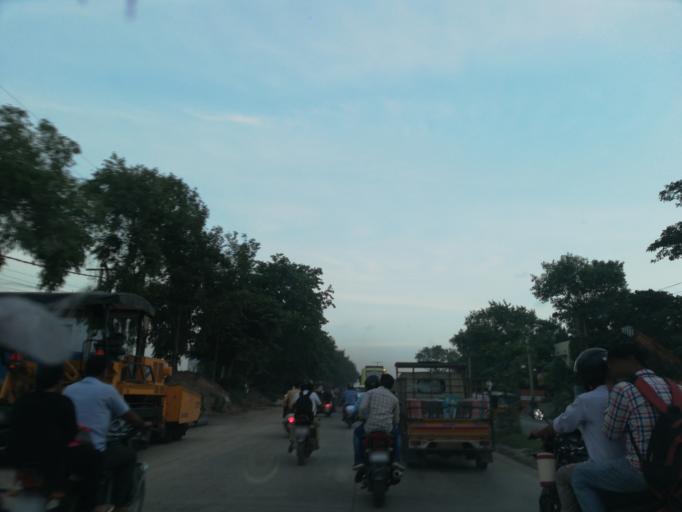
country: IN
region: Telangana
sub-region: Medak
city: Serilingampalle
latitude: 17.5216
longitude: 78.3565
